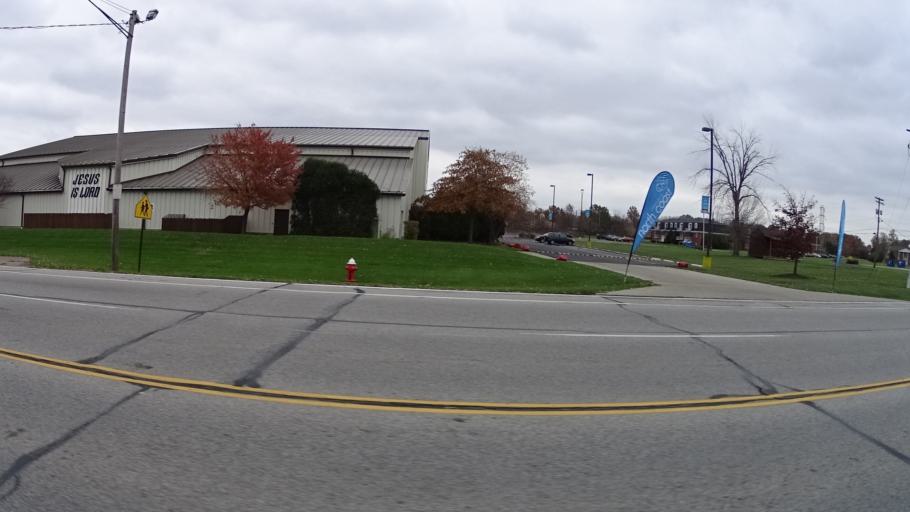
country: US
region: Ohio
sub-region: Lorain County
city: Lorain
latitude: 41.4319
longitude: -82.2026
